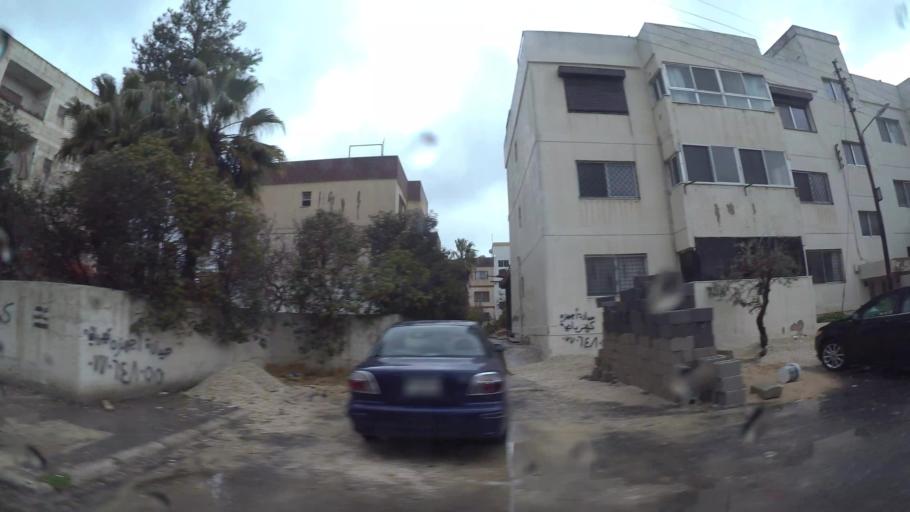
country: JO
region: Amman
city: Al Jubayhah
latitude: 32.0313
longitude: 35.8749
